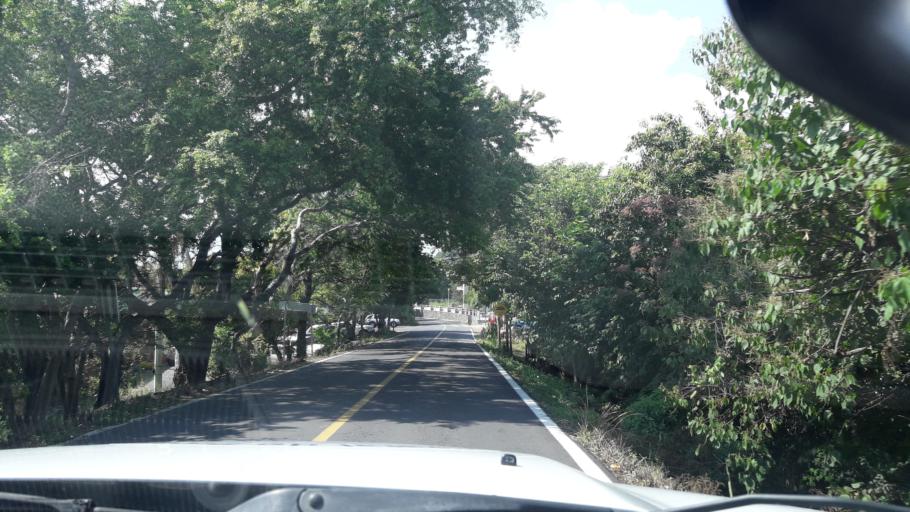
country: MX
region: Colima
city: Comala
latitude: 19.3316
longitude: -103.7508
